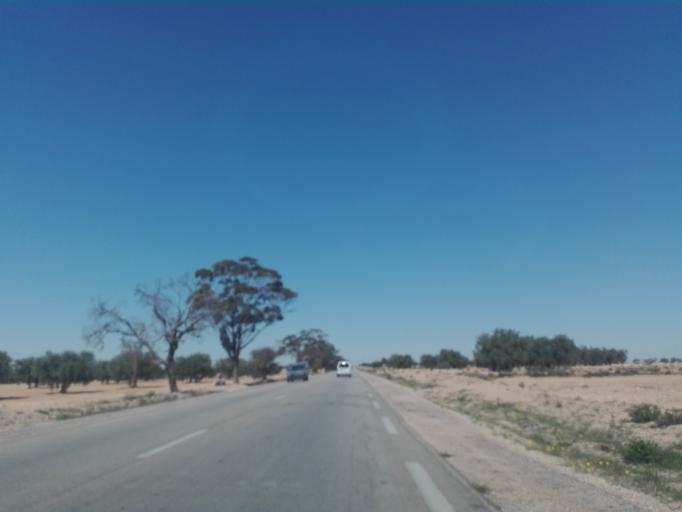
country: TN
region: Safaqis
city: Bi'r `Ali Bin Khalifah
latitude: 34.7518
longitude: 10.3431
